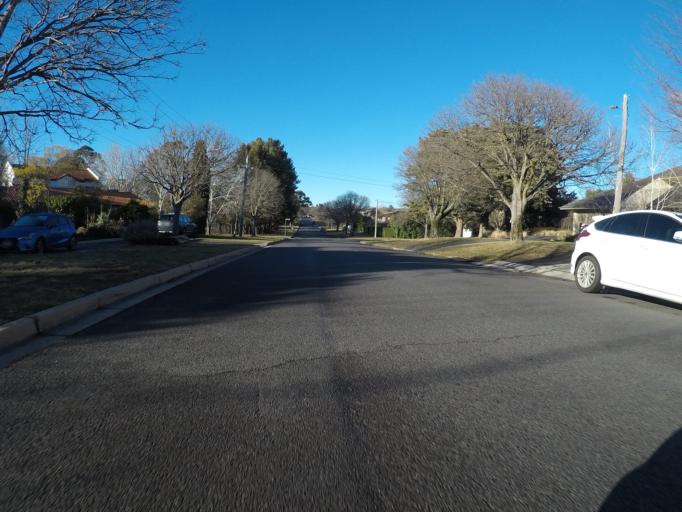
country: AU
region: Australian Capital Territory
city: Forrest
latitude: -35.3051
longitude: 149.0996
